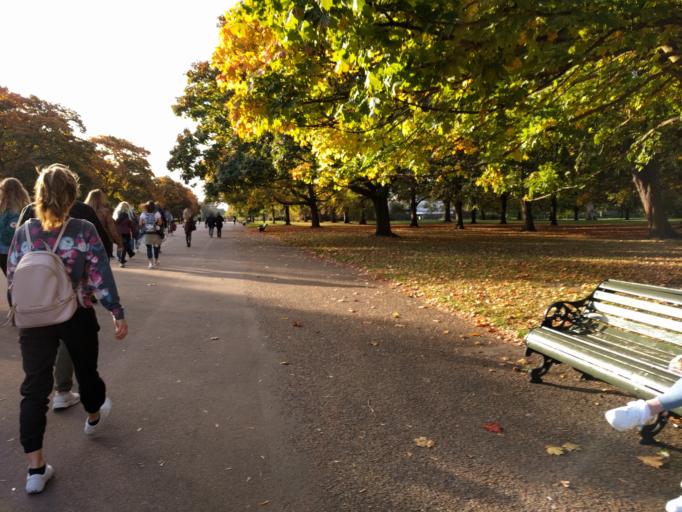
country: GB
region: England
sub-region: Greater London
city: Bayswater
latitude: 51.5081
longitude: -0.1870
